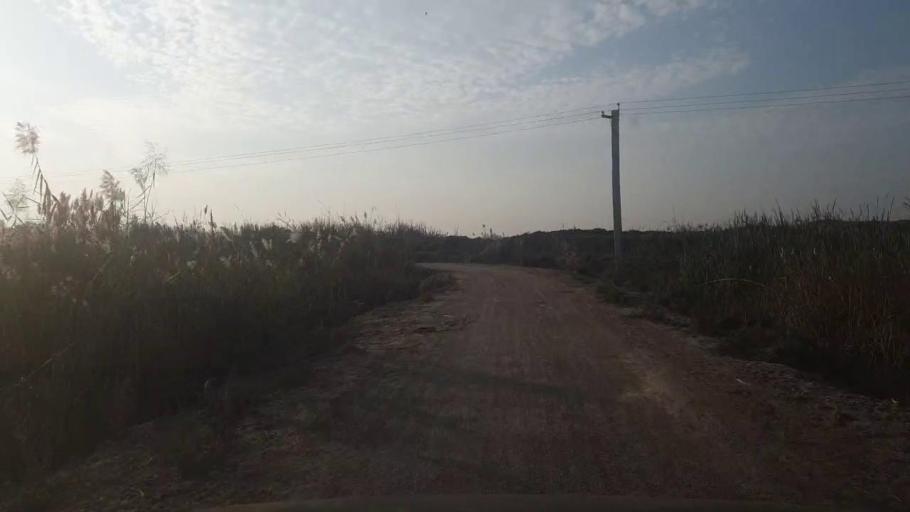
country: PK
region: Sindh
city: Sakrand
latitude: 26.0996
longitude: 68.3990
